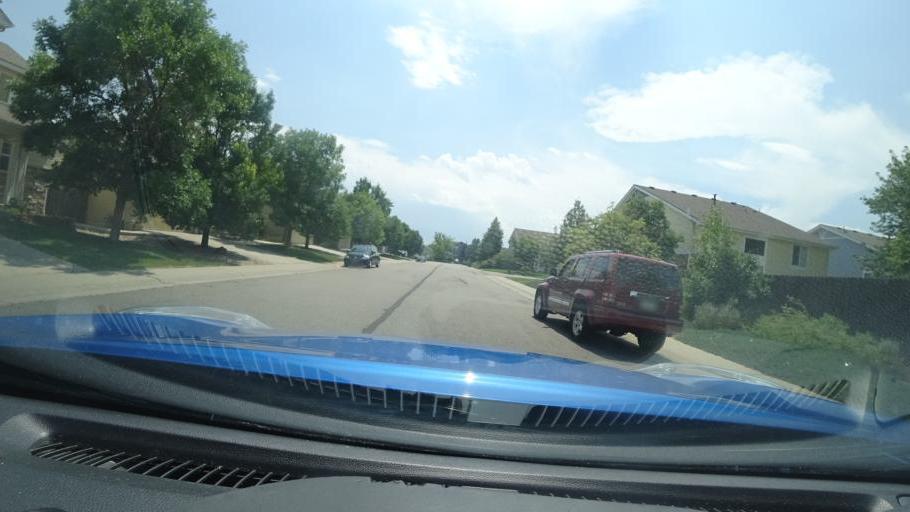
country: US
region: Colorado
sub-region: Adams County
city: Aurora
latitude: 39.6720
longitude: -104.7550
